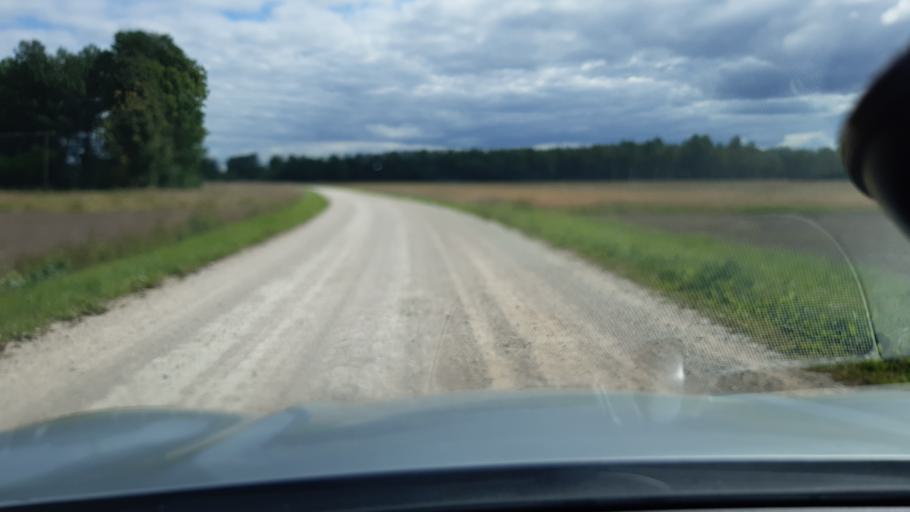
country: EE
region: Paernumaa
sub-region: Vaendra vald (alev)
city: Vandra
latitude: 58.7932
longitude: 24.9810
